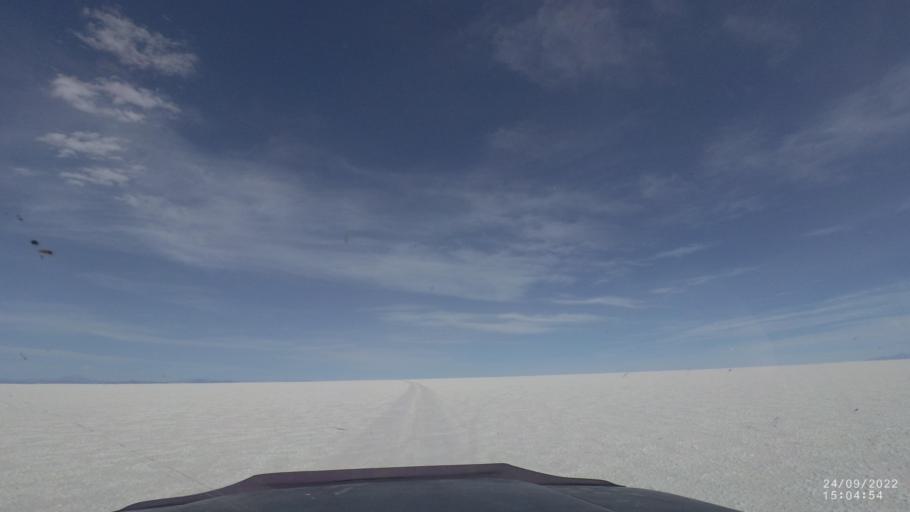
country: BO
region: Potosi
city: Colchani
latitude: -19.9027
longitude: -67.5211
